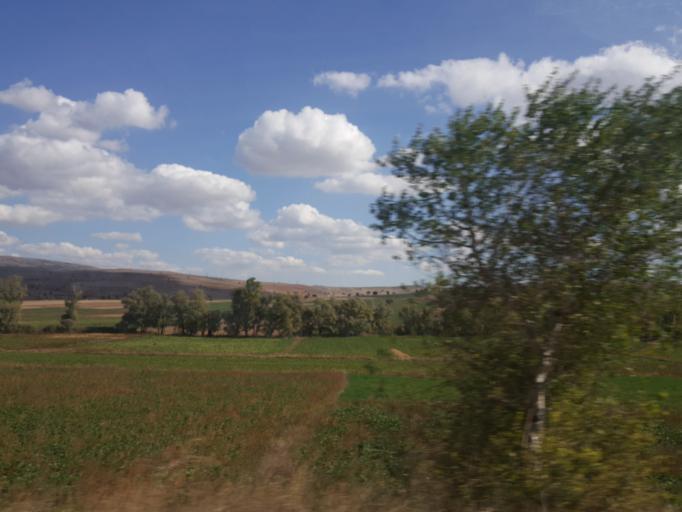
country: TR
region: Tokat
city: Camlibel
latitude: 40.1799
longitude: 36.4470
